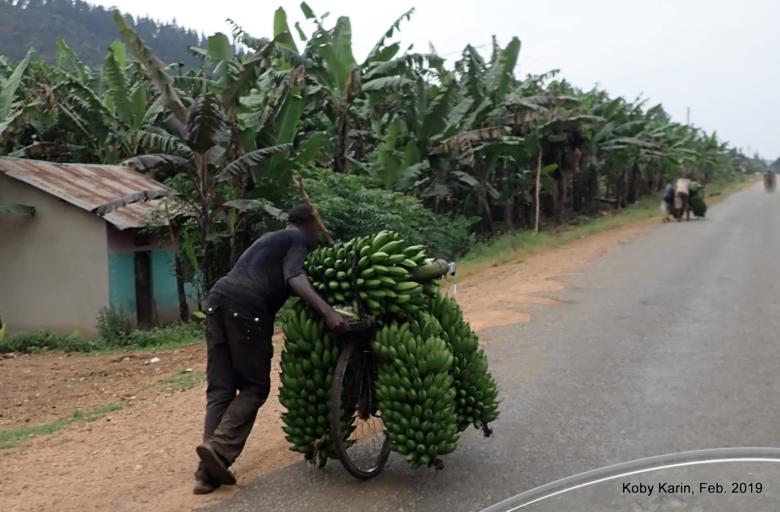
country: UG
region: Western Region
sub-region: Rubirizi District
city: Rubirizi
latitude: -0.3107
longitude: 30.1042
